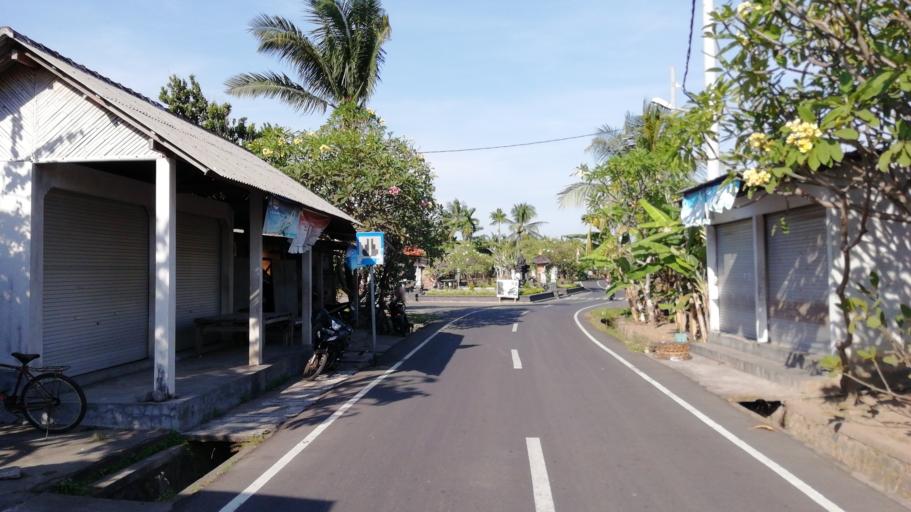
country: ID
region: Bali
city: Banjar Pasekan
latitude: -8.6104
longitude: 115.2892
